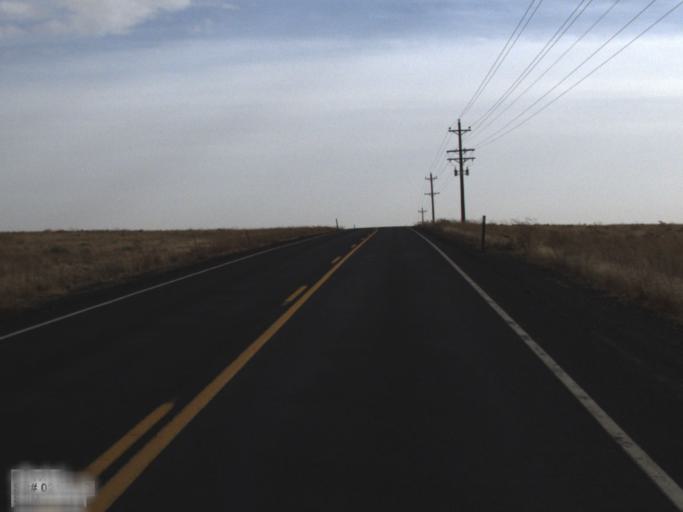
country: US
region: Washington
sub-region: Adams County
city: Ritzville
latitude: 47.4288
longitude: -118.7153
